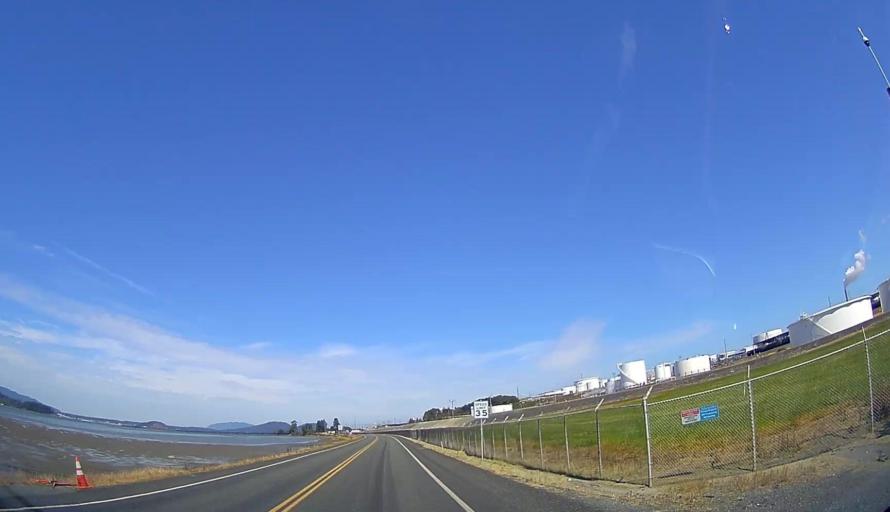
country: US
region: Washington
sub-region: Skagit County
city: Anacortes
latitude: 48.4664
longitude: -122.5706
